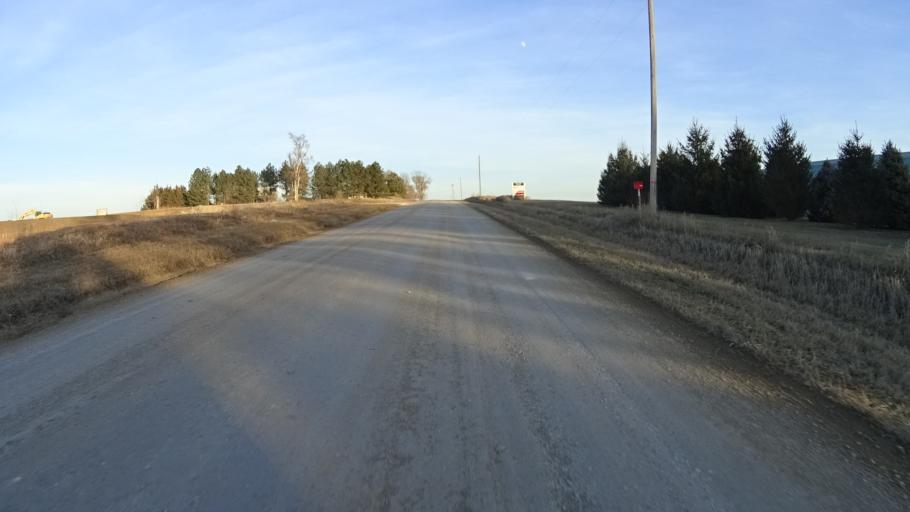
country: US
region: Nebraska
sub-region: Sarpy County
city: Springfield
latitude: 41.1326
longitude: -96.1067
